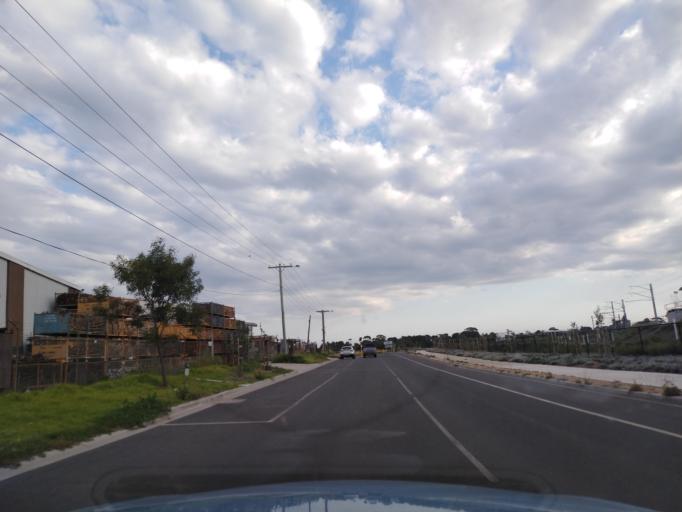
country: AU
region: Victoria
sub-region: Hobsons Bay
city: Seaholme
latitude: -37.8544
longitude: 144.8527
